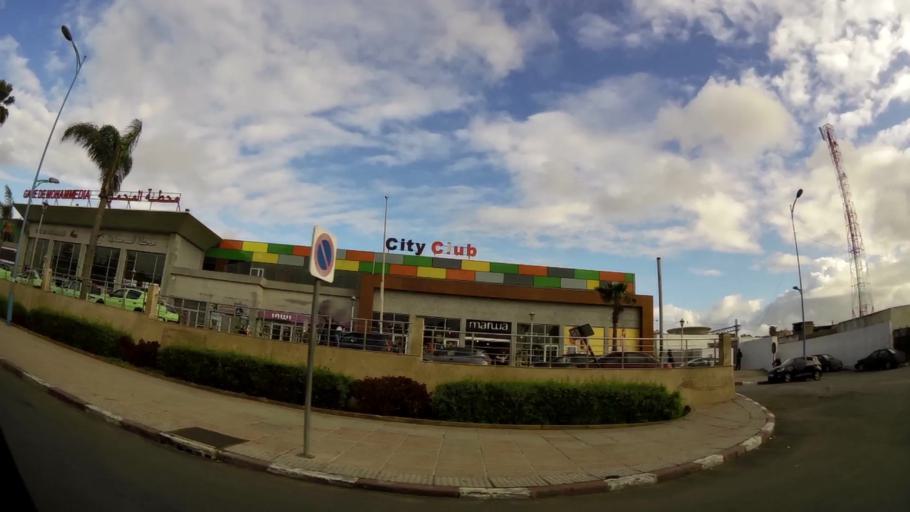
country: MA
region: Grand Casablanca
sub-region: Mohammedia
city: Mohammedia
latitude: 33.6958
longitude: -7.3883
